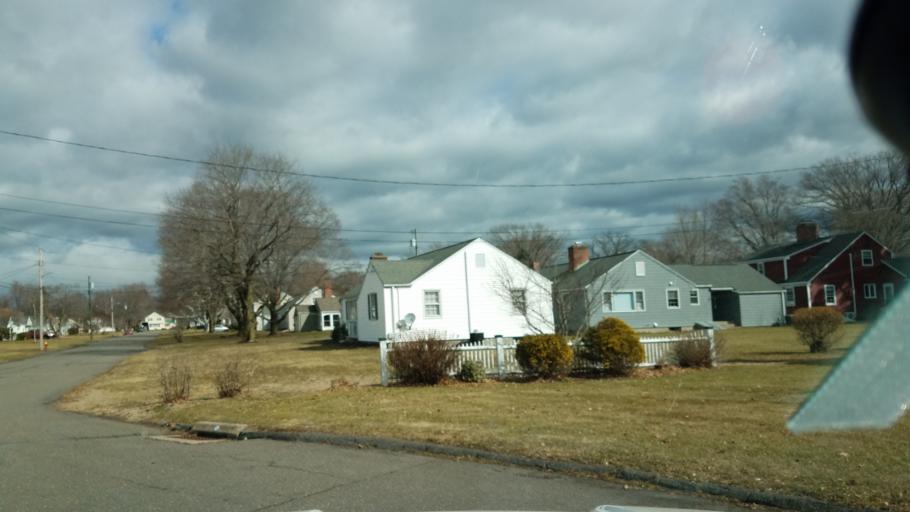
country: US
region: Connecticut
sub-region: Hartford County
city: Wethersfield
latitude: 41.7049
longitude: -72.6565
